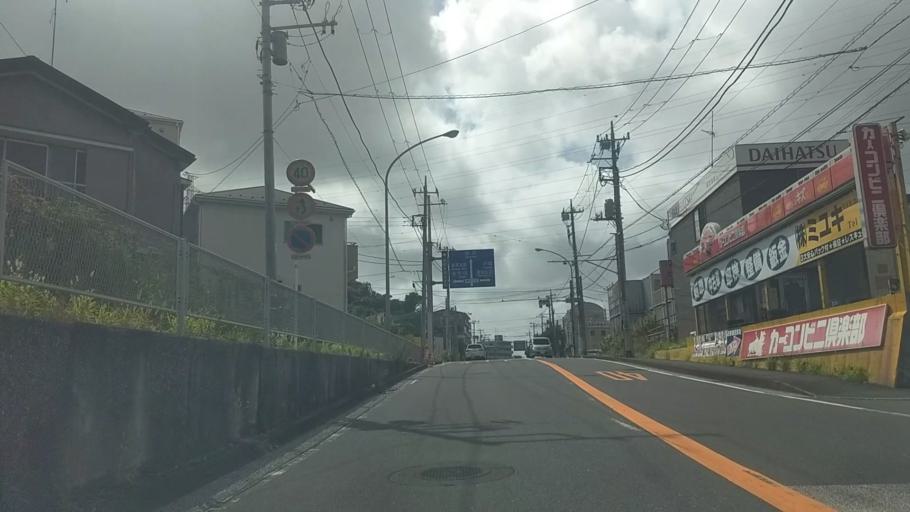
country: JP
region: Kanagawa
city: Yokohama
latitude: 35.3781
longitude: 139.6084
